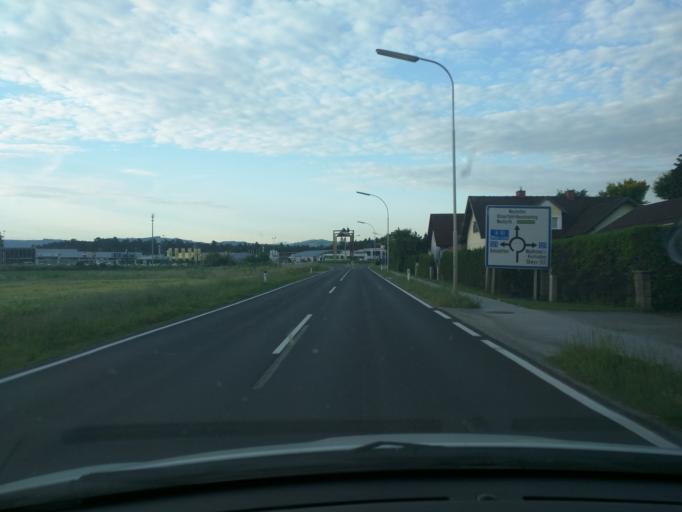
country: AT
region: Lower Austria
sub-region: Politischer Bezirk Amstetten
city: Winklarn
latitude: 48.0847
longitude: 14.8015
